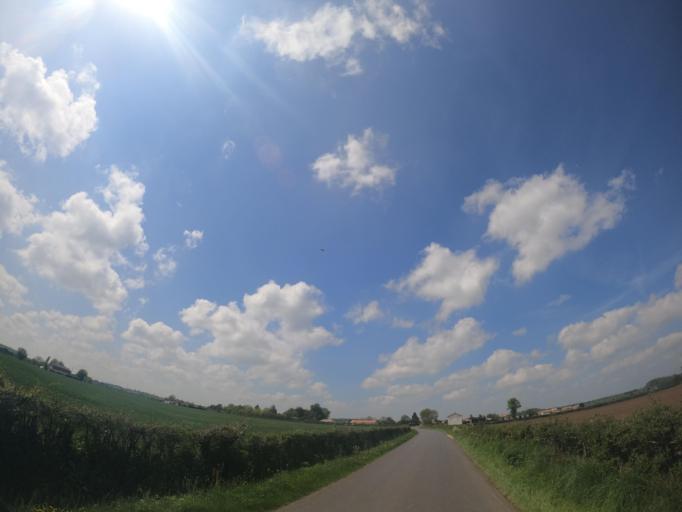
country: FR
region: Poitou-Charentes
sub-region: Departement des Deux-Sevres
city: Saint-Varent
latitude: 46.8590
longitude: -0.2386
